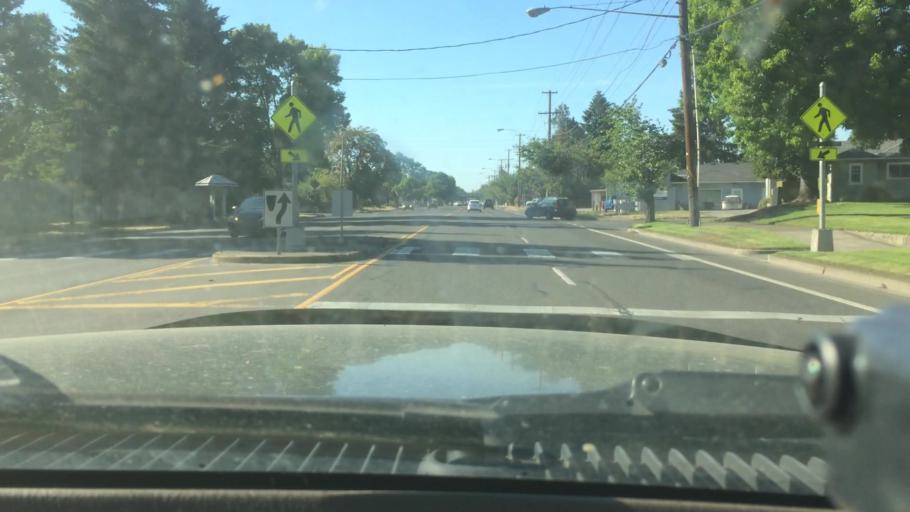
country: US
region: Oregon
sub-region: Lane County
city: Eugene
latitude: 44.0917
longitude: -123.1263
